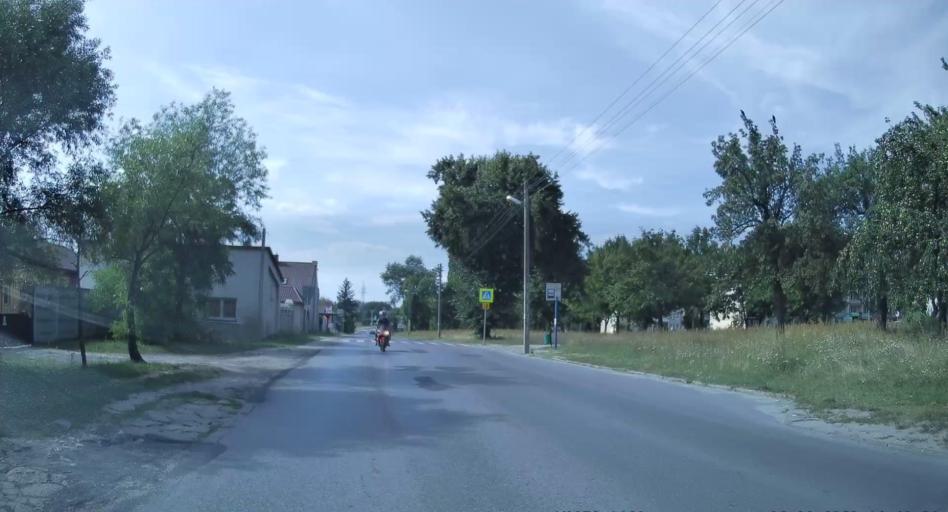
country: PL
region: Lodz Voivodeship
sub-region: Powiat tomaszowski
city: Tomaszow Mazowiecki
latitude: 51.5424
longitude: 19.9968
